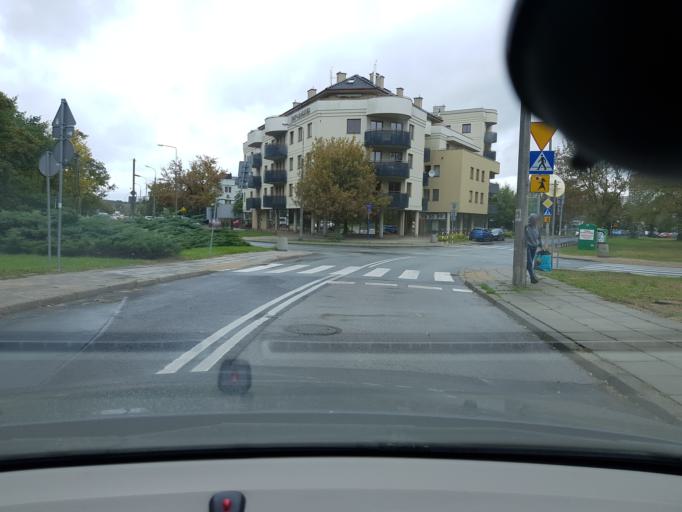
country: PL
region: Masovian Voivodeship
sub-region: Warszawa
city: Zoliborz
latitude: 52.2775
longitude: 20.9689
